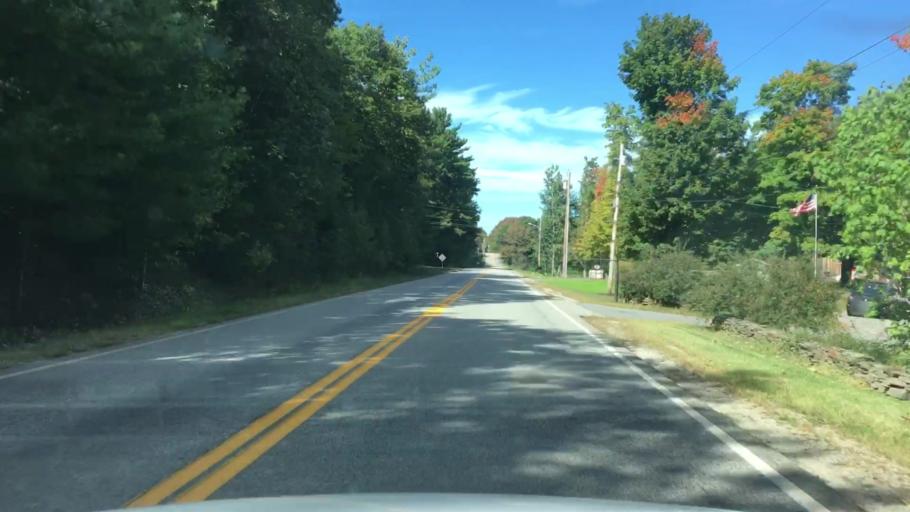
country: US
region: Maine
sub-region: Cumberland County
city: West Scarborough
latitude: 43.6148
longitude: -70.4055
